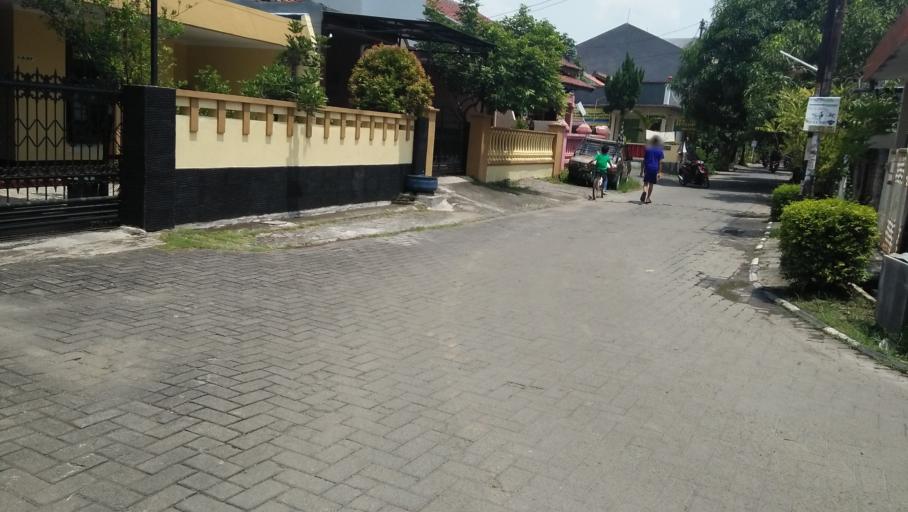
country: ID
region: Central Java
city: Semarang
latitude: -7.0285
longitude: 110.4615
